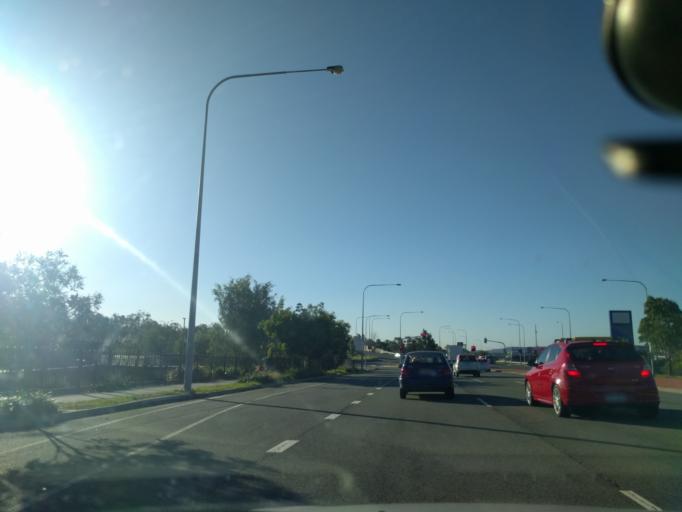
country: AU
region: Queensland
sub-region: Brisbane
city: Richlands
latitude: -27.5952
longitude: 152.9487
